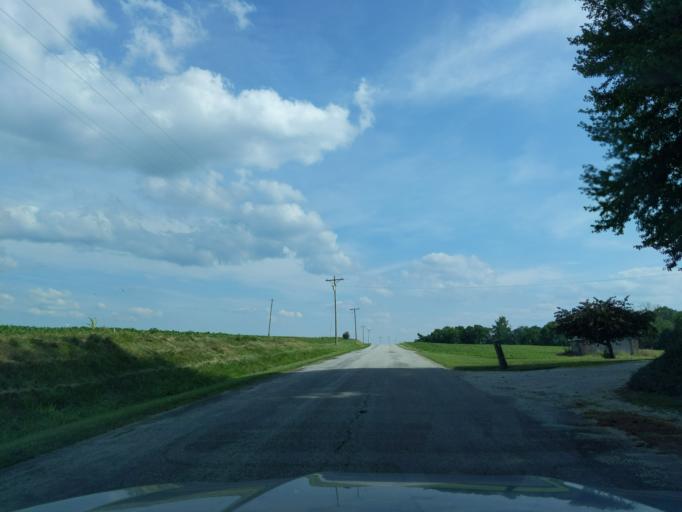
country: US
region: Indiana
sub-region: Decatur County
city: Greensburg
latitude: 39.2844
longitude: -85.4662
